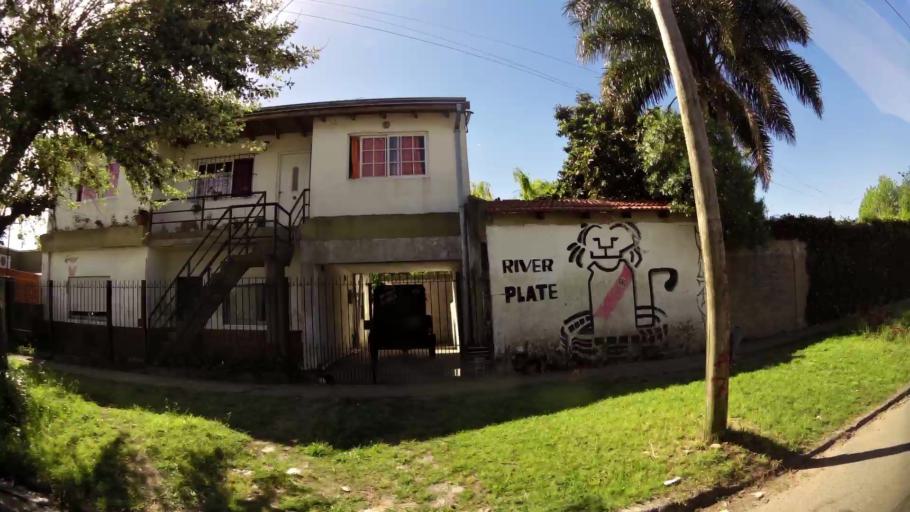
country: AR
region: Buenos Aires
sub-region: Partido de Almirante Brown
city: Adrogue
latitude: -34.8009
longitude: -58.3567
